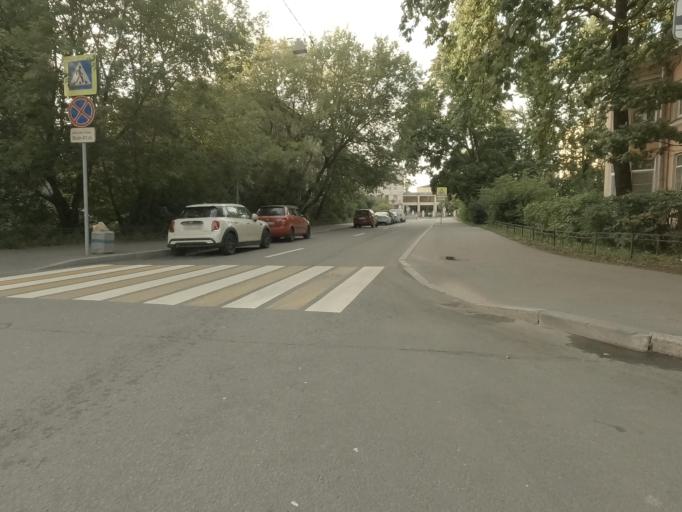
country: RU
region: St.-Petersburg
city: Admiralteisky
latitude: 59.8968
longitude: 30.2681
